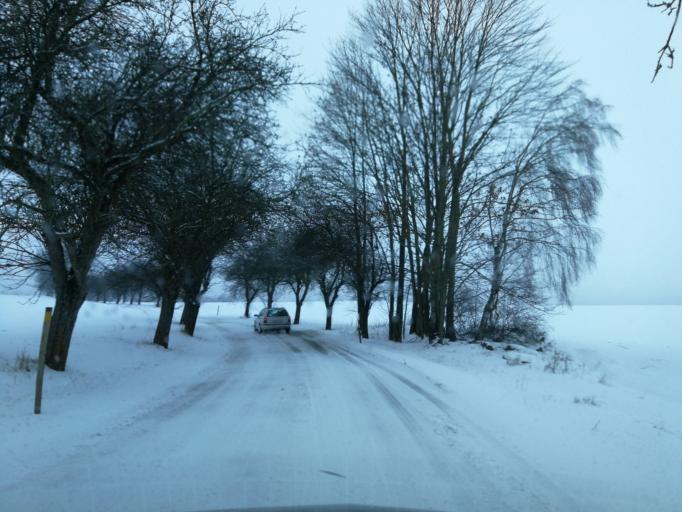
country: CZ
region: Vysocina
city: Heralec
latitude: 49.5332
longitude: 15.4301
